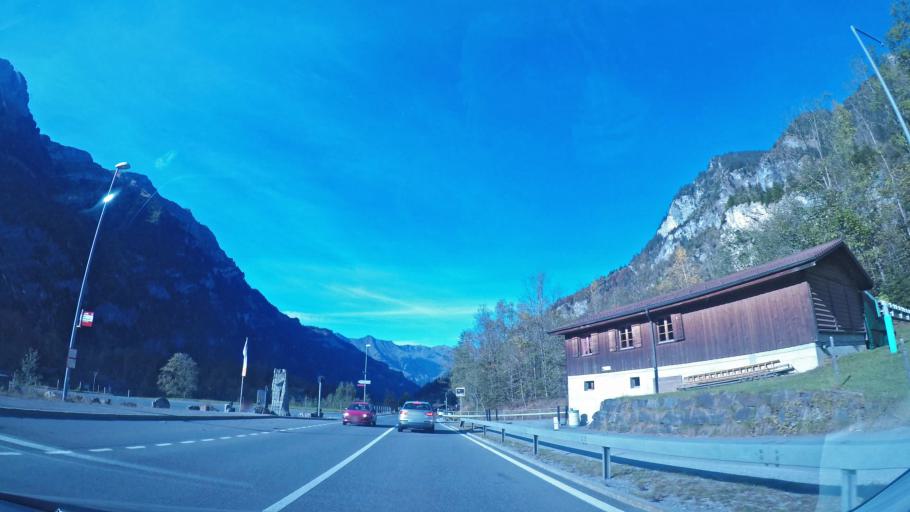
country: CH
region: Bern
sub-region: Frutigen-Niedersimmental District
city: Kandersteg
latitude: 46.5198
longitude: 7.6790
